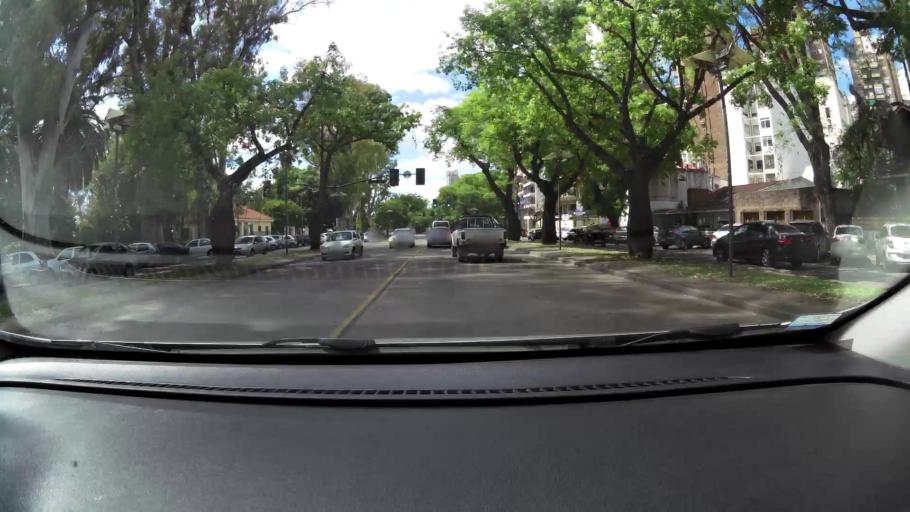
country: AR
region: Santa Fe
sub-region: Departamento de Rosario
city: Rosario
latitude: -32.9445
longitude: -60.6331
